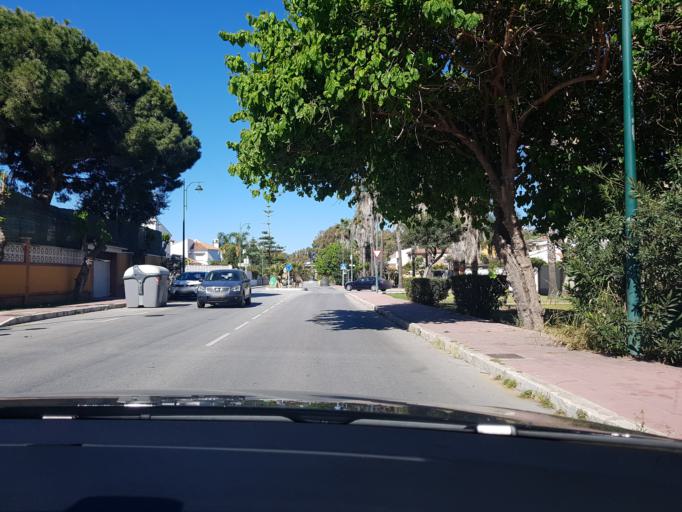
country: ES
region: Andalusia
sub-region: Provincia de Malaga
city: Torremolinos
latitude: 36.6680
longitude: -4.4626
